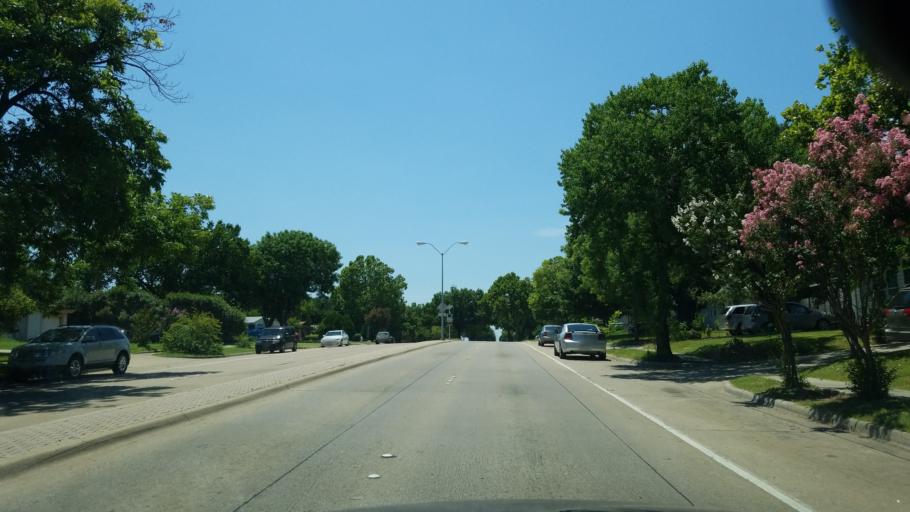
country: US
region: Texas
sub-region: Dallas County
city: Farmers Branch
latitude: 32.9387
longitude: -96.8937
